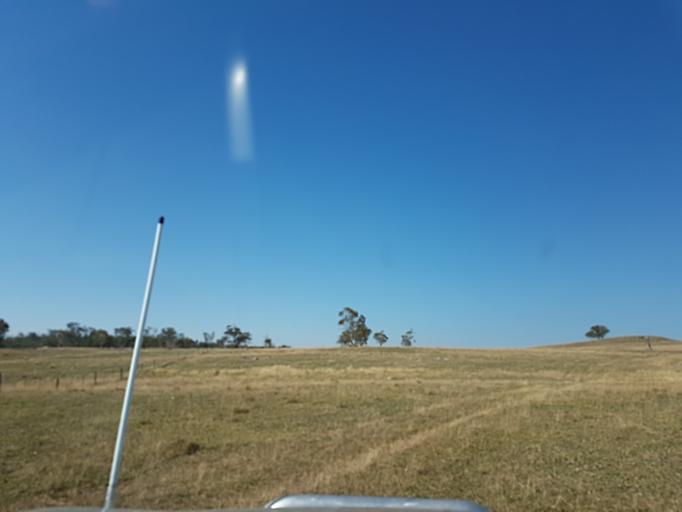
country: AU
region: New South Wales
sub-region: Snowy River
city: Jindabyne
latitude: -37.0454
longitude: 148.2967
